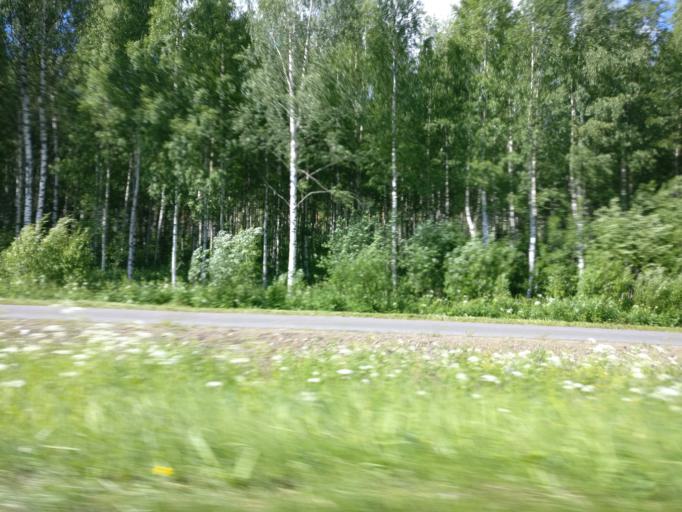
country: FI
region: Southern Savonia
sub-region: Savonlinna
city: Savonlinna
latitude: 61.8797
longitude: 29.0198
